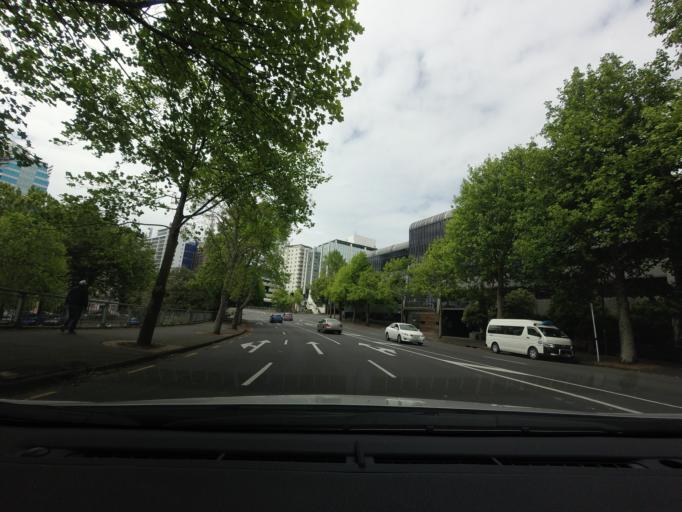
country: NZ
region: Auckland
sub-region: Auckland
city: Auckland
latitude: -36.8531
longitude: 174.7614
